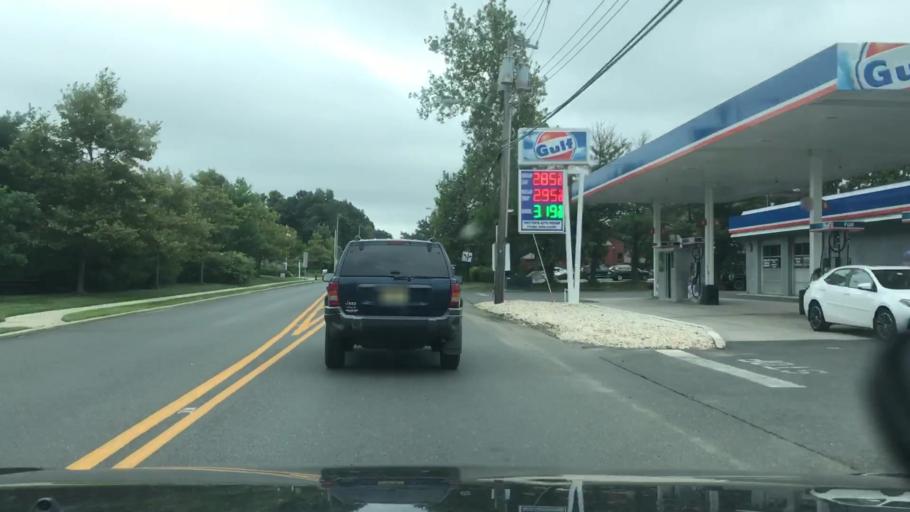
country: US
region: New Jersey
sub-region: Monmouth County
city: West Long Branch
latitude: 40.2931
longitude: -74.0272
